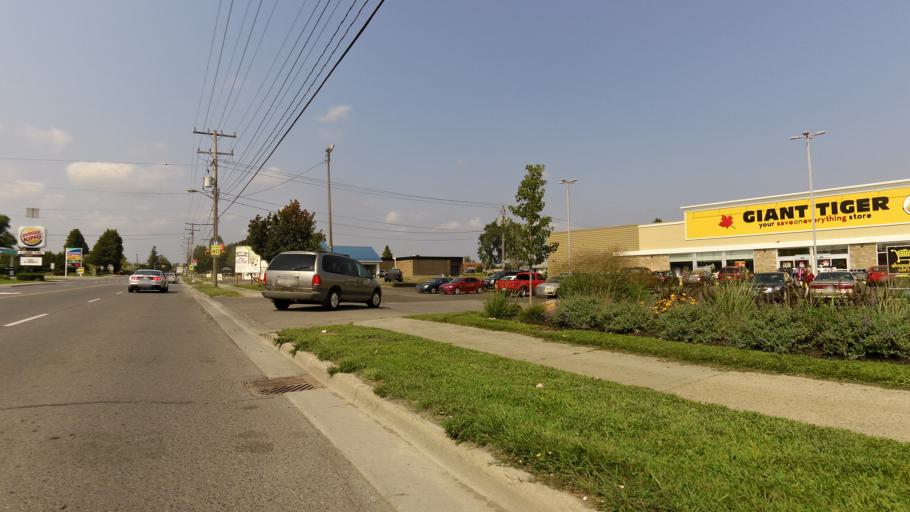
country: CA
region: Ontario
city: Prescott
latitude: 44.7173
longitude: -75.5204
